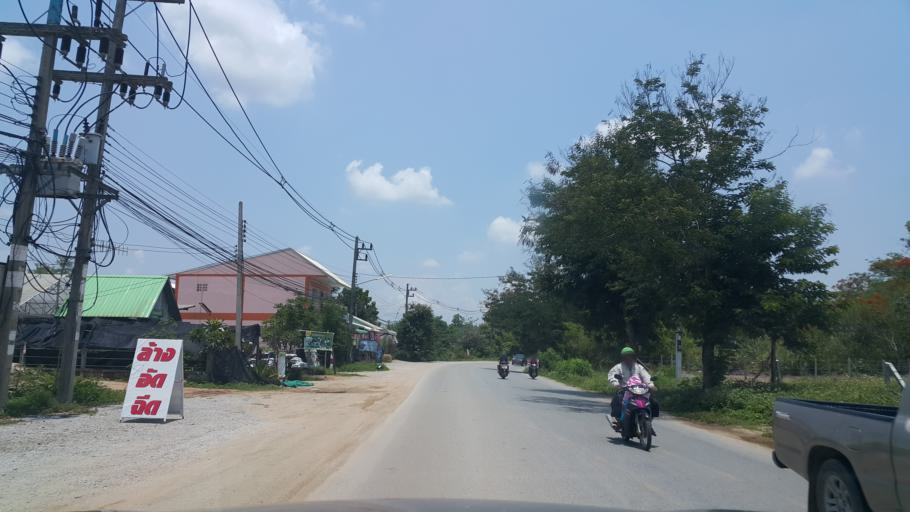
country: TH
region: Chiang Rai
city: Chiang Rai
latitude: 19.9339
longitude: 99.8131
